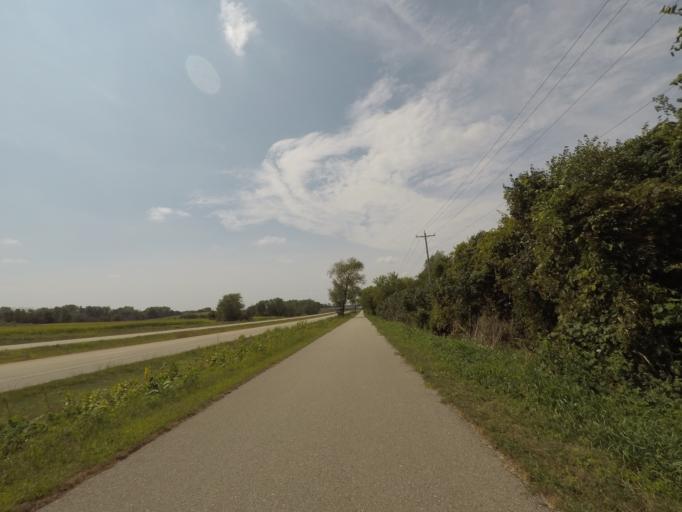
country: US
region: Wisconsin
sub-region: Jefferson County
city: Lake Koshkonong
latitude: 42.8722
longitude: -88.8902
